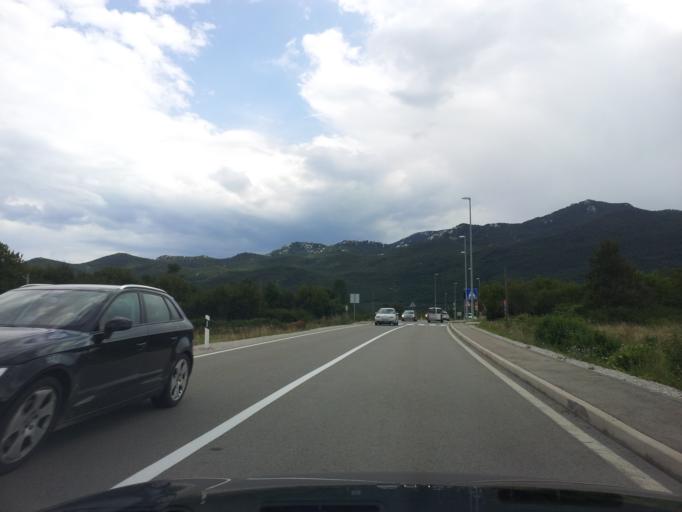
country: HR
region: Zadarska
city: Gracac
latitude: 44.3019
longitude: 15.8612
